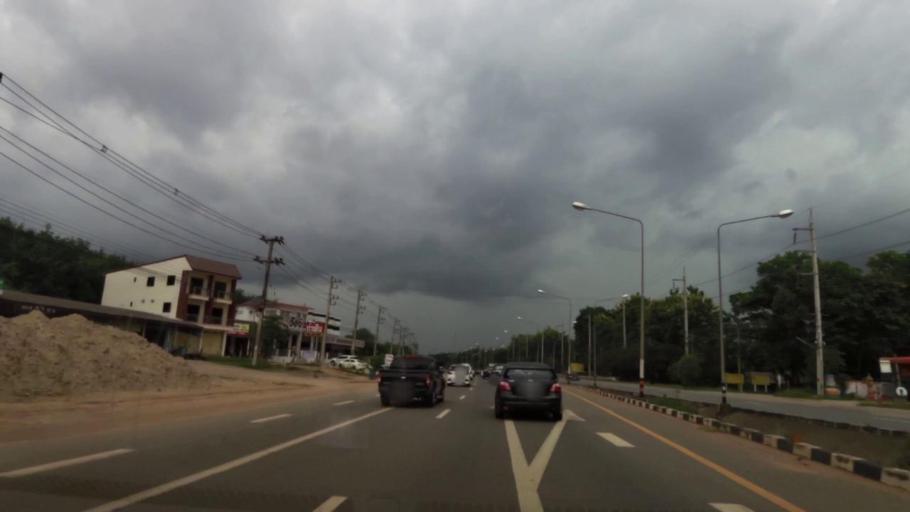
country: TH
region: Rayong
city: Wang Chan
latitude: 12.9428
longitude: 101.5191
